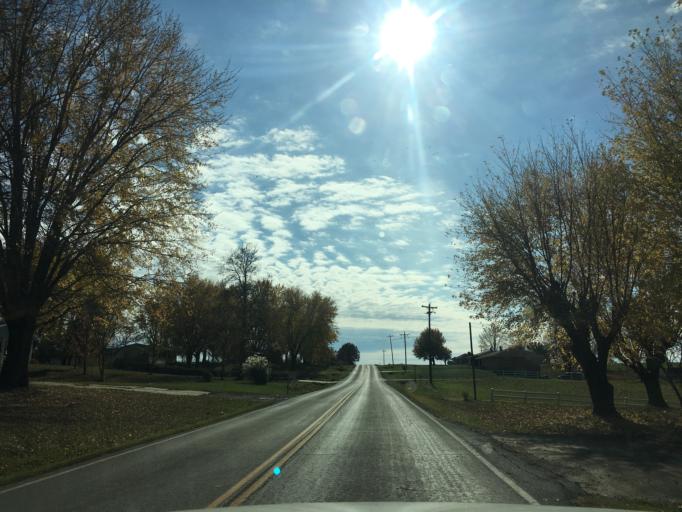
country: US
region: Missouri
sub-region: Osage County
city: Linn
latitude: 38.4574
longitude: -91.8349
